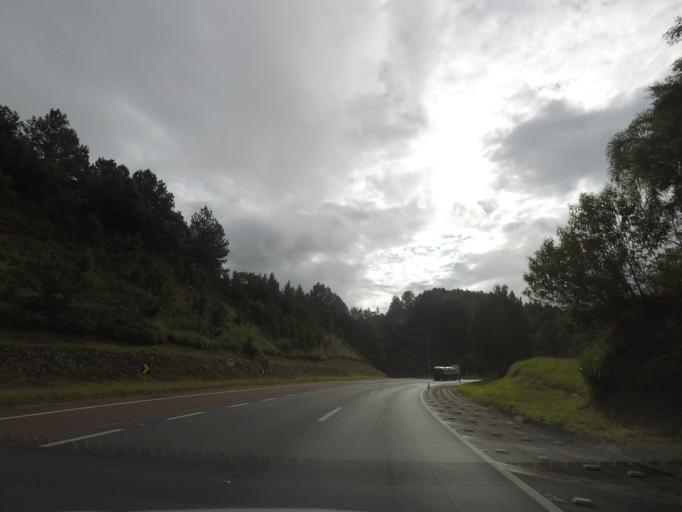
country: BR
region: Parana
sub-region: Campina Grande Do Sul
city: Campina Grande do Sul
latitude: -25.1852
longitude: -48.8847
